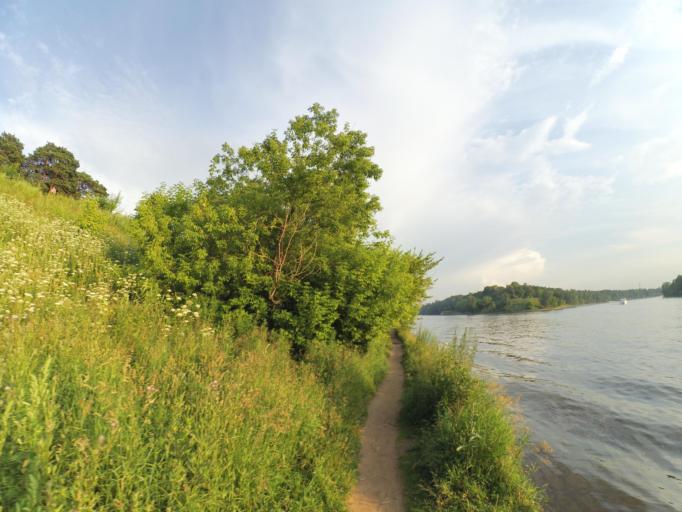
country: RU
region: Moscow
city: Shchukino
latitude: 55.7929
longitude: 37.4467
